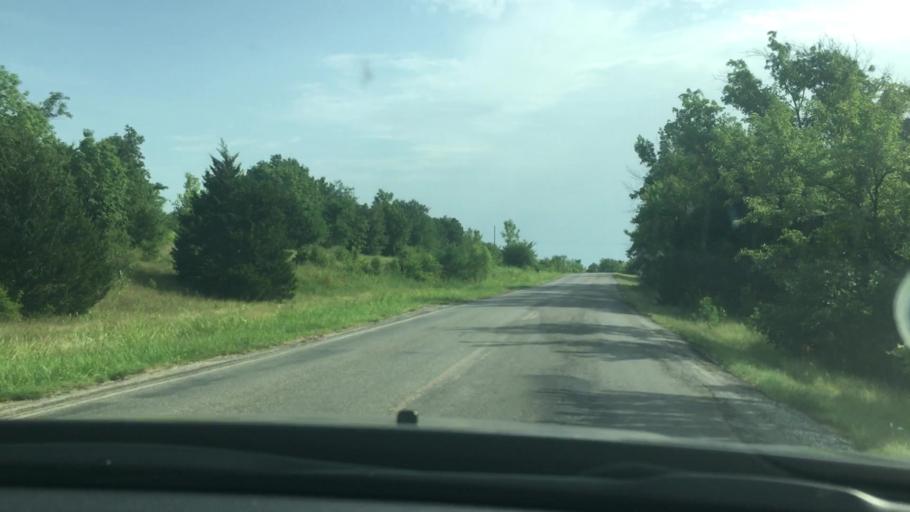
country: US
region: Oklahoma
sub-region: Pontotoc County
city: Byng
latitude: 34.8678
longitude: -96.5987
